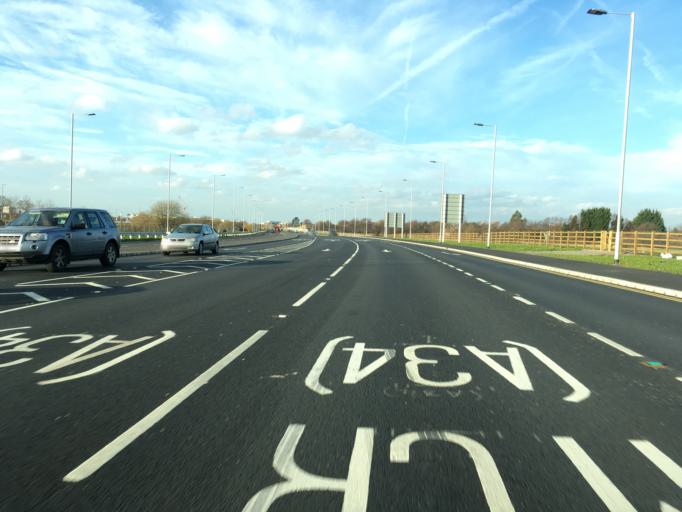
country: GB
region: England
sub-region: Cheshire East
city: Wilmslow
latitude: 53.3626
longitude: -2.2441
